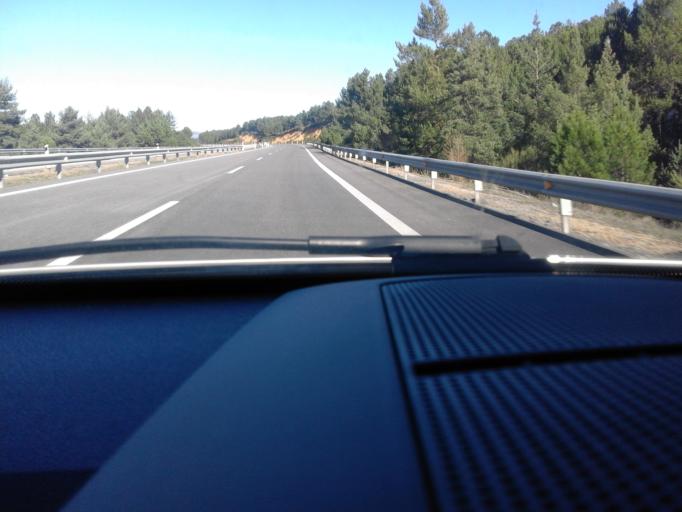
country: ES
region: Castille and Leon
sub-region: Provincia de Leon
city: Cimanes del Tejar
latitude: 42.6544
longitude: -5.7508
